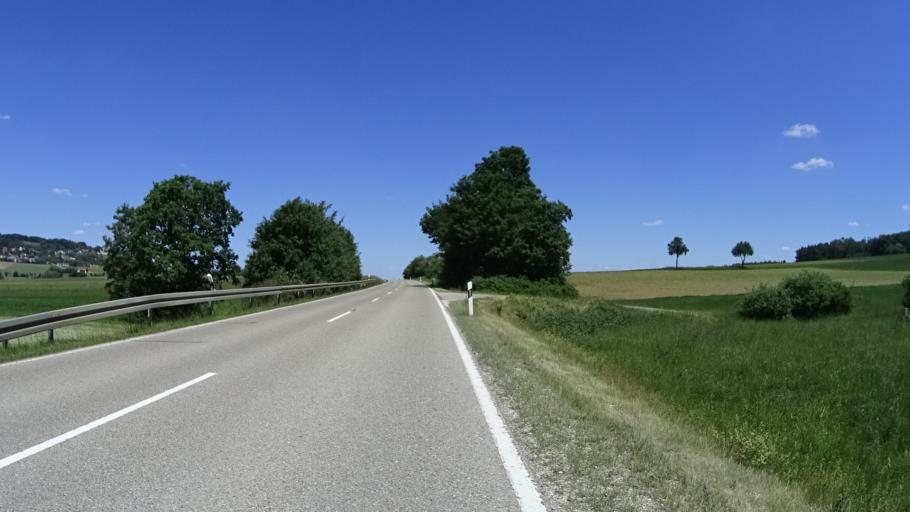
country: DE
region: Bavaria
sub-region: Regierungsbezirk Mittelfranken
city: Bergen
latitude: 49.0923
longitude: 11.1041
